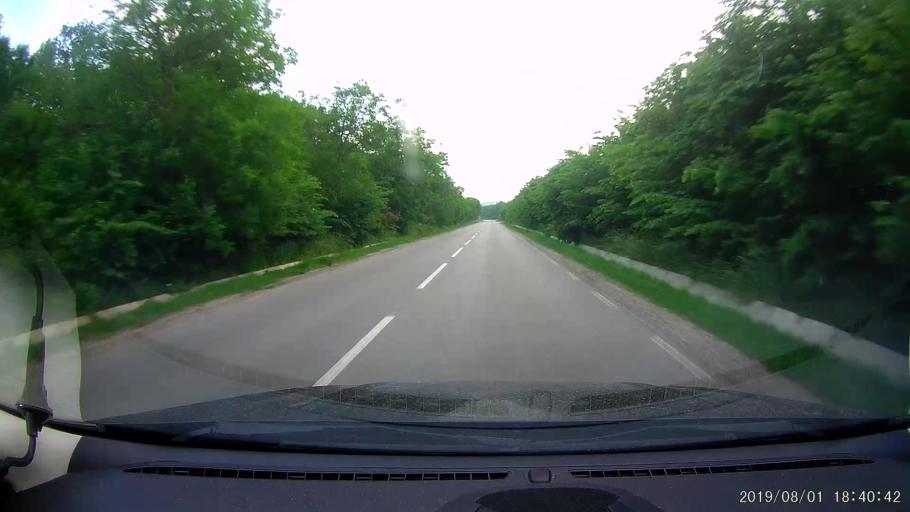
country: BG
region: Shumen
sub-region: Obshtina Khitrino
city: Gara Khitrino
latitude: 43.3610
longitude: 26.9204
